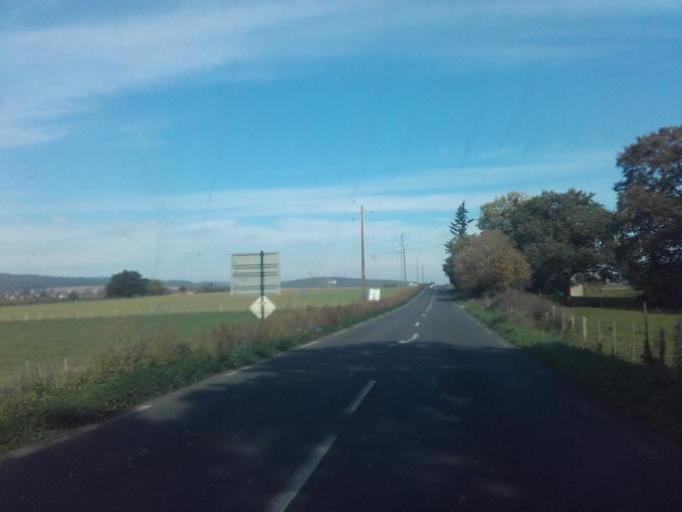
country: FR
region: Bourgogne
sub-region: Departement de Saone-et-Loire
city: Dracy-le-Fort
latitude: 46.8188
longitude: 4.7520
